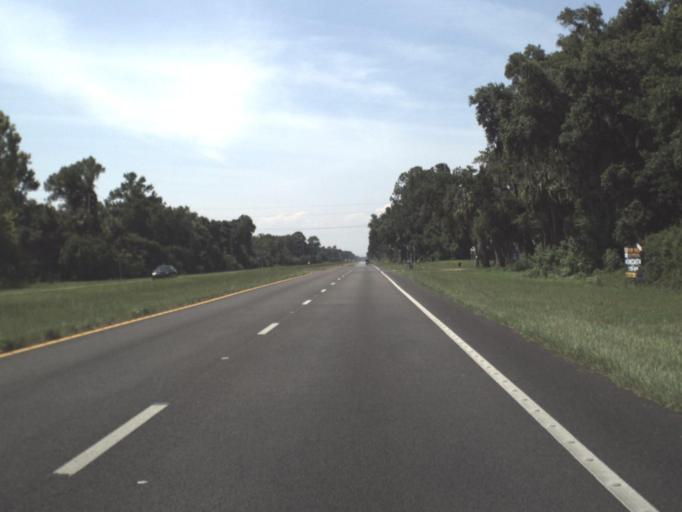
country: US
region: Florida
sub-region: Citrus County
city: Crystal River
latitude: 28.9271
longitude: -82.6140
